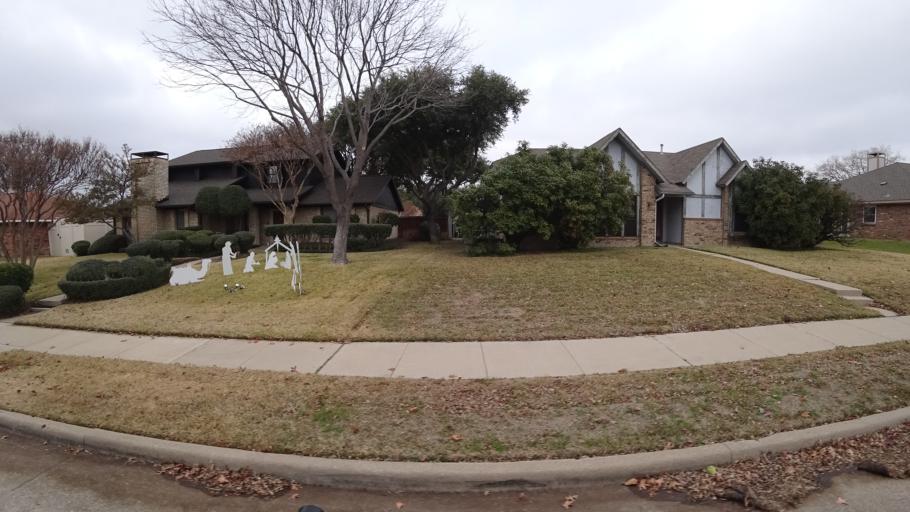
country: US
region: Texas
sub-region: Denton County
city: Lewisville
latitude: 33.0430
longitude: -97.0395
